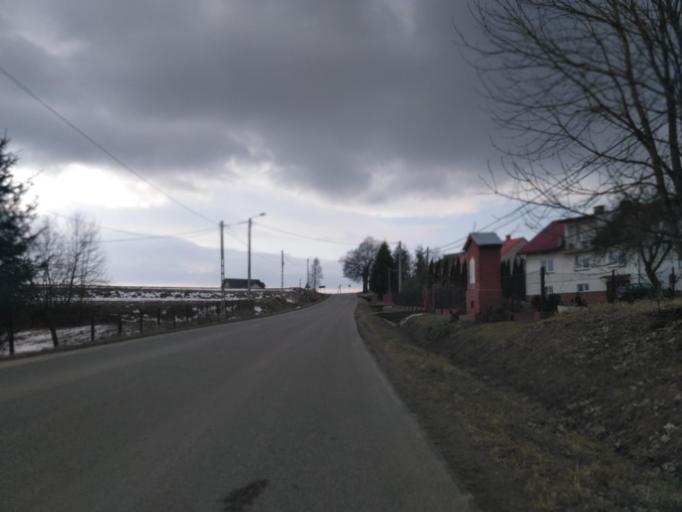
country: PL
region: Subcarpathian Voivodeship
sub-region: Powiat sanocki
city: Strachocina
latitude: 49.6061
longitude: 22.1433
